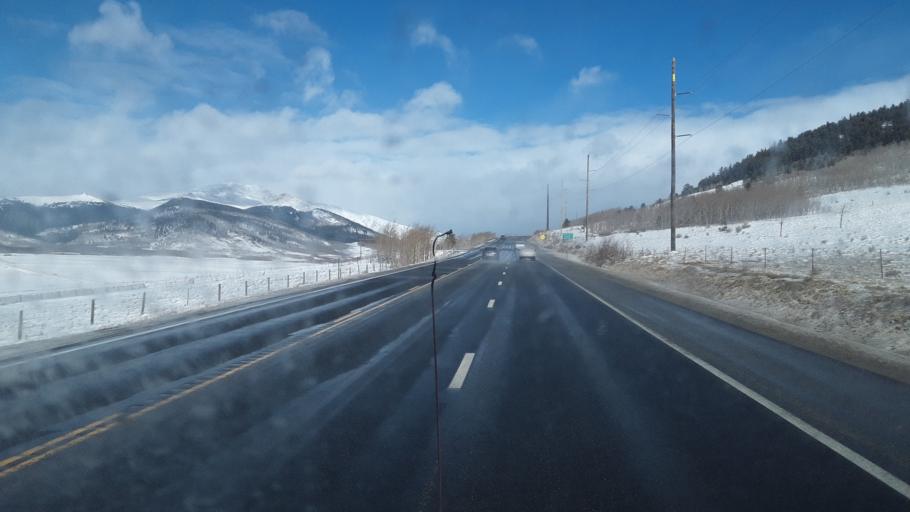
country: US
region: Colorado
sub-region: Park County
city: Fairplay
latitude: 39.2512
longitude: -105.9632
